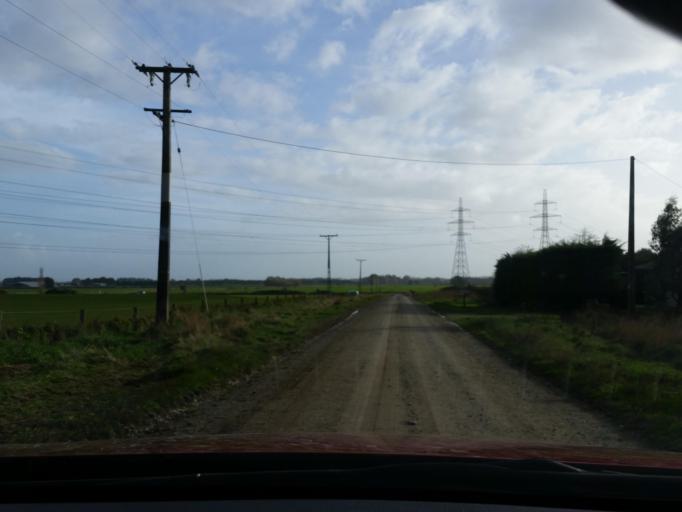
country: NZ
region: Southland
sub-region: Southland District
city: Winton
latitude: -46.2726
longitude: 168.3213
